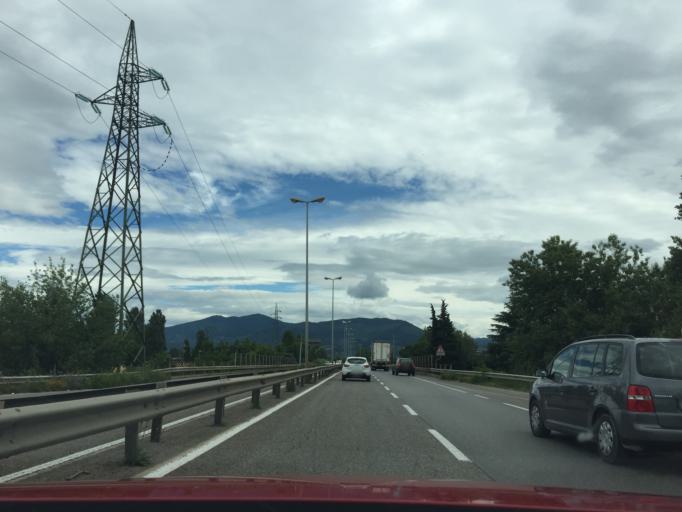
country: IT
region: Tuscany
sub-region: Province of Florence
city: Mantignano-Ugnano
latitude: 43.7816
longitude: 11.1870
